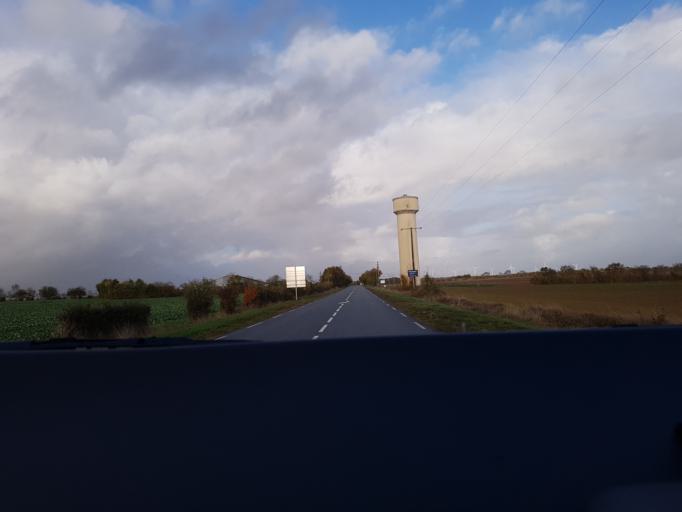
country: FR
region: Poitou-Charentes
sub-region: Departement des Deux-Sevres
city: Brioux-sur-Boutonne
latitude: 46.1292
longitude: -0.2316
